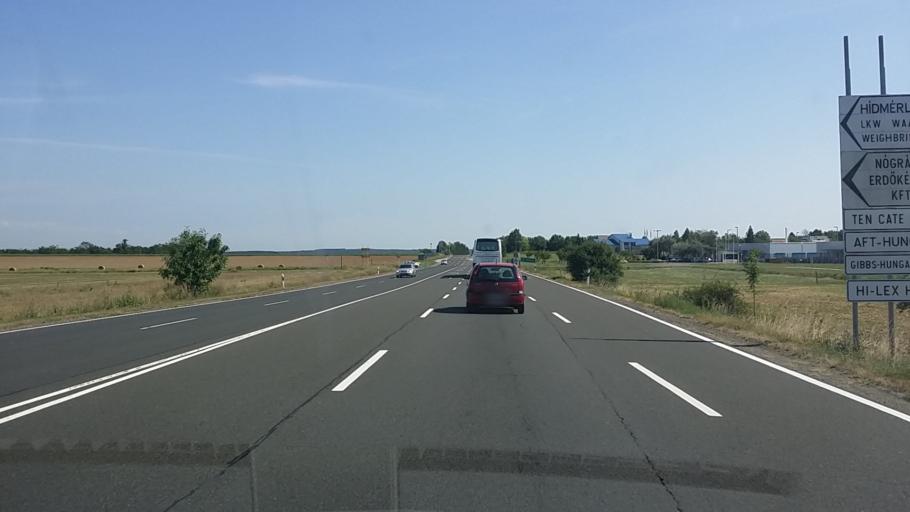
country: HU
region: Nograd
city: Retsag
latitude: 47.9173
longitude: 19.1174
